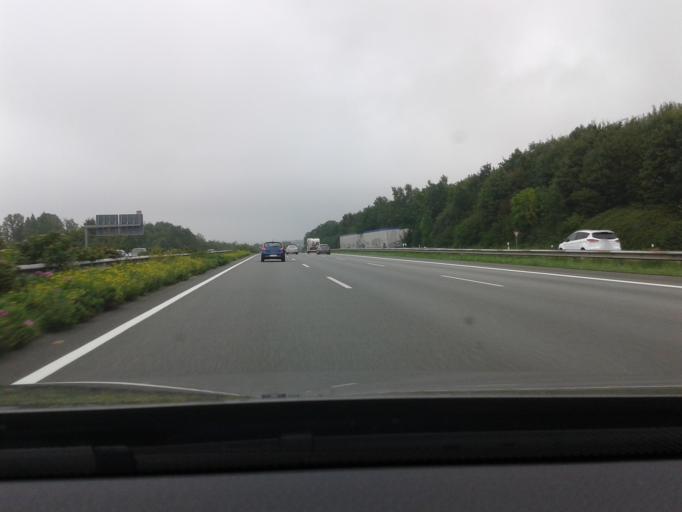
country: DE
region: North Rhine-Westphalia
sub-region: Regierungsbezirk Detmold
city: Oerlinghausen
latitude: 51.9966
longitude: 8.6191
